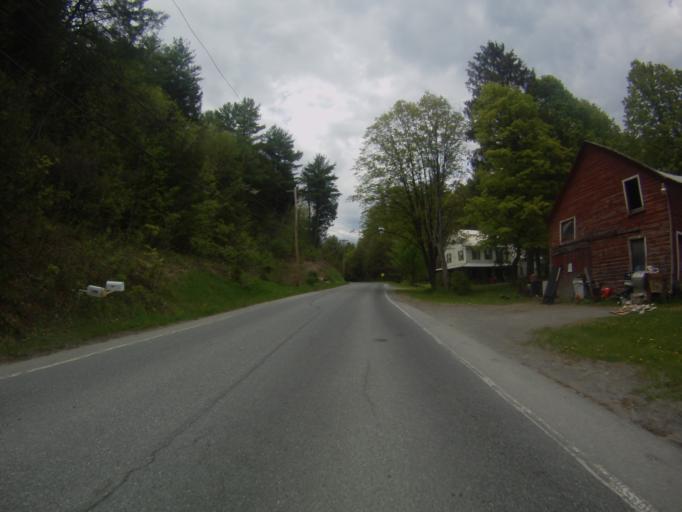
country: US
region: New York
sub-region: Essex County
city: Ticonderoga
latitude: 43.9427
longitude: -73.4697
